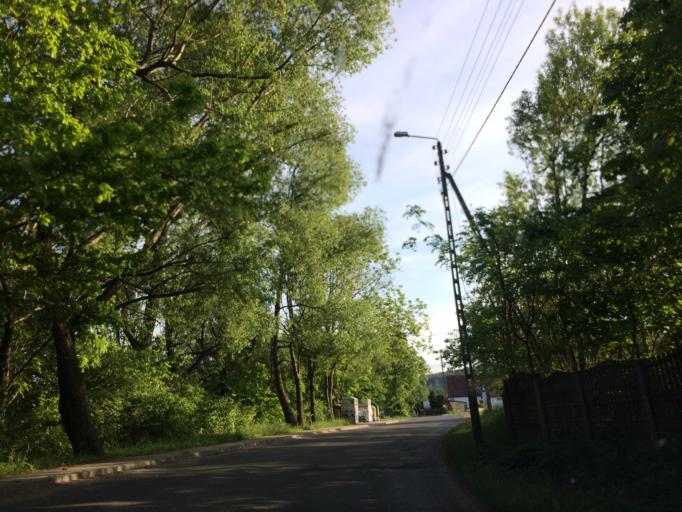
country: PL
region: Lower Silesian Voivodeship
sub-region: Powiat swidnicki
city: Swidnica
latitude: 50.7769
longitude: 16.5028
